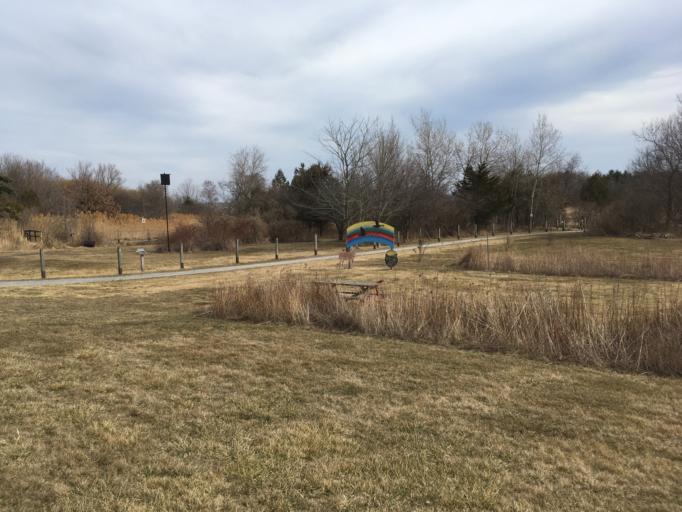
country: CA
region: Ontario
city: Oshawa
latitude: 43.8754
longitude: -78.8032
